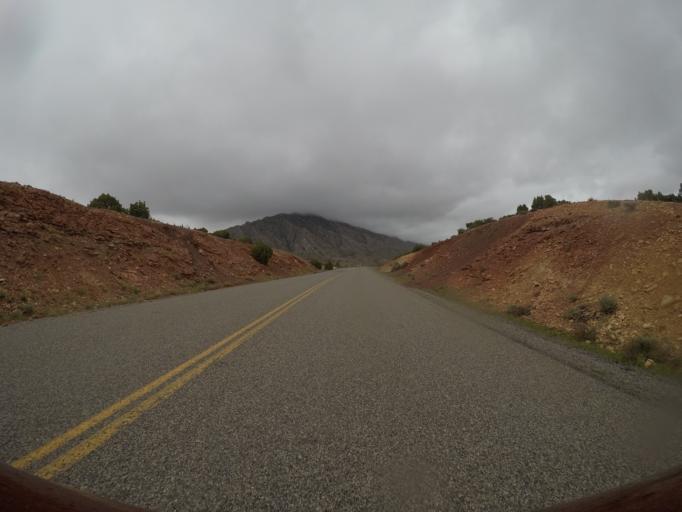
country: US
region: Wyoming
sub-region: Big Horn County
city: Lovell
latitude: 45.0233
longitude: -108.2544
